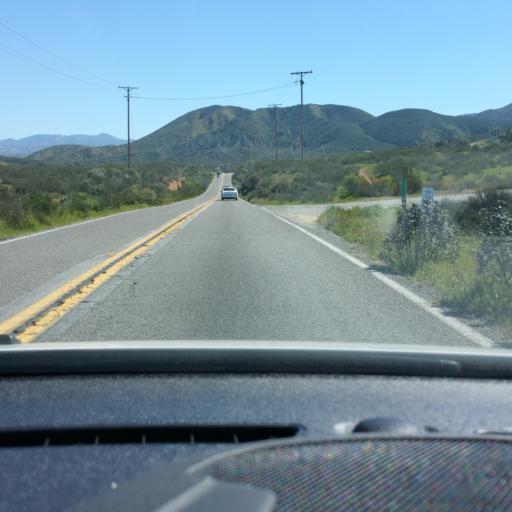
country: US
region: California
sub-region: Riverside County
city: Aguanga
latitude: 33.4676
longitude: -116.9871
